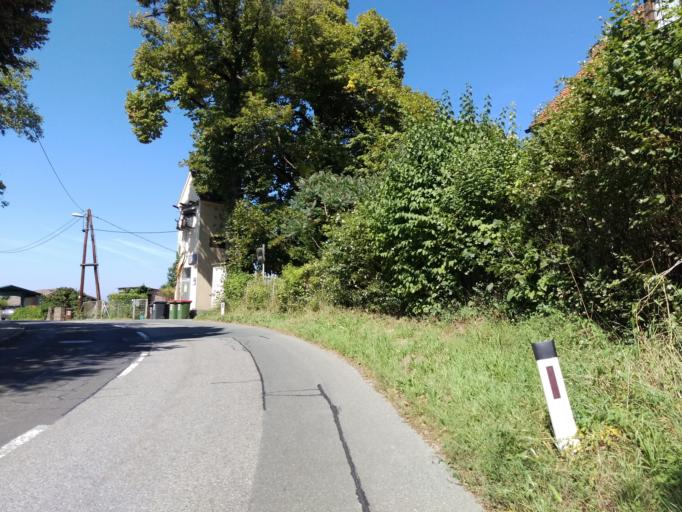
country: AT
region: Styria
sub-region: Politischer Bezirk Graz-Umgebung
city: Hart bei Graz
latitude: 47.0691
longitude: 15.5048
